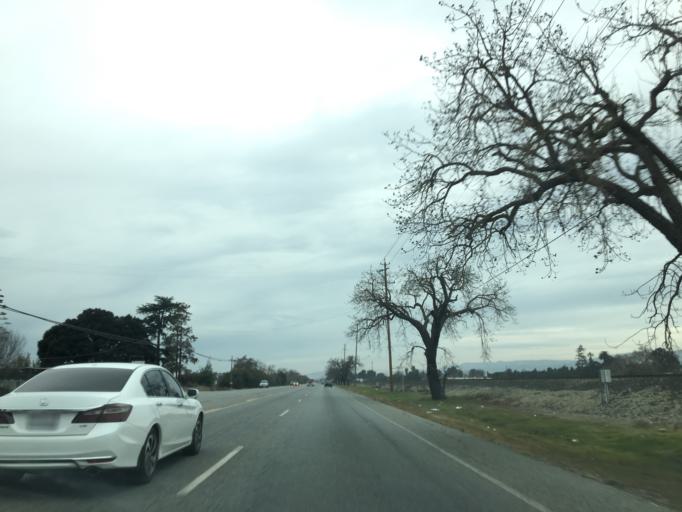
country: US
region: California
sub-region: Santa Clara County
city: San Martin
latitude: 37.0467
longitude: -121.5888
